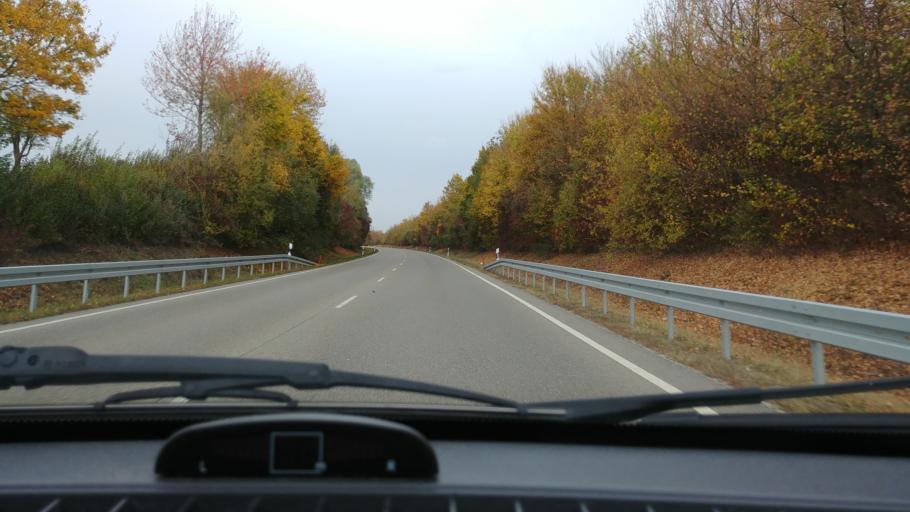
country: DE
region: Baden-Wuerttemberg
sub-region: Regierungsbezirk Stuttgart
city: Satteldorf
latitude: 49.1617
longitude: 10.0754
